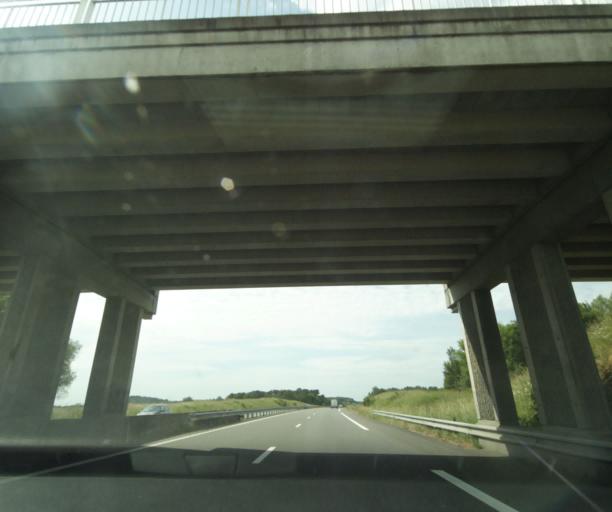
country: FR
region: Pays de la Loire
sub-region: Departement de Maine-et-Loire
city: Maze
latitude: 47.4930
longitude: -0.2727
